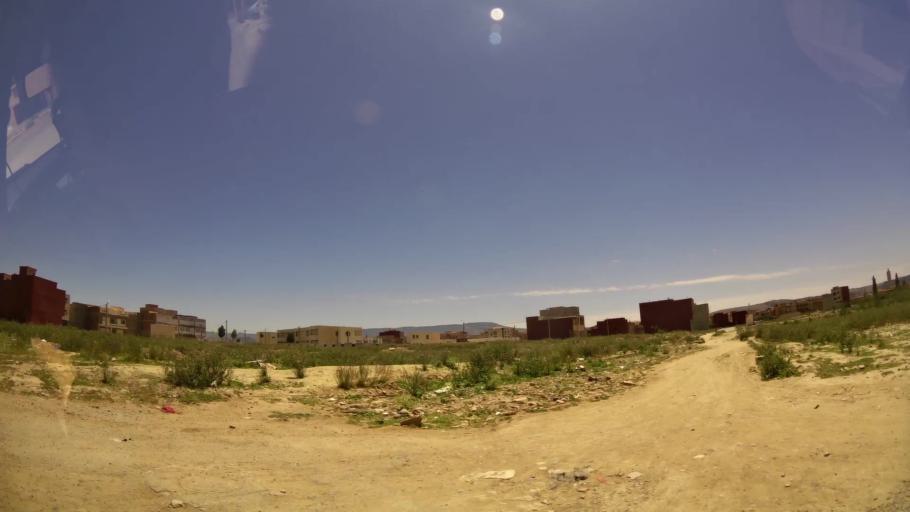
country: MA
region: Oriental
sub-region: Oujda-Angad
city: Oujda
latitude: 34.6746
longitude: -1.8686
